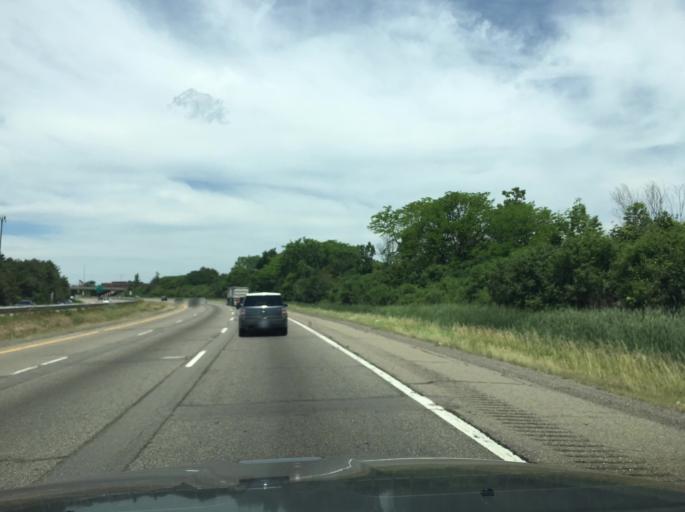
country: US
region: Michigan
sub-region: Oakland County
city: Troy
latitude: 42.6021
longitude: -83.1644
